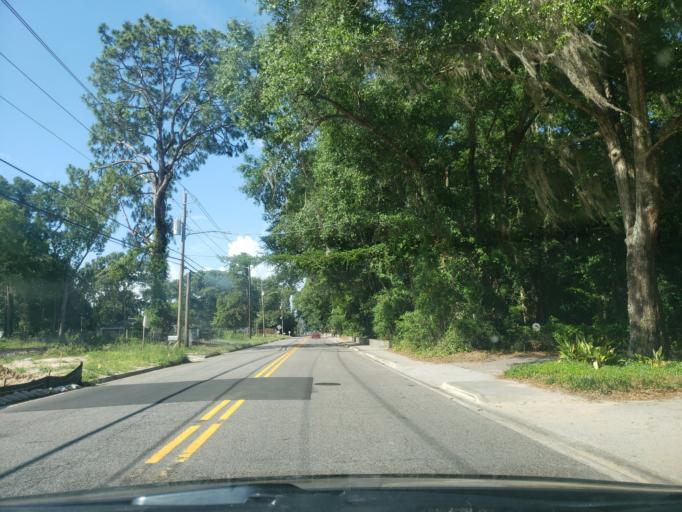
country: US
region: Georgia
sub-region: Chatham County
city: Georgetown
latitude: 31.9875
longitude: -81.1669
